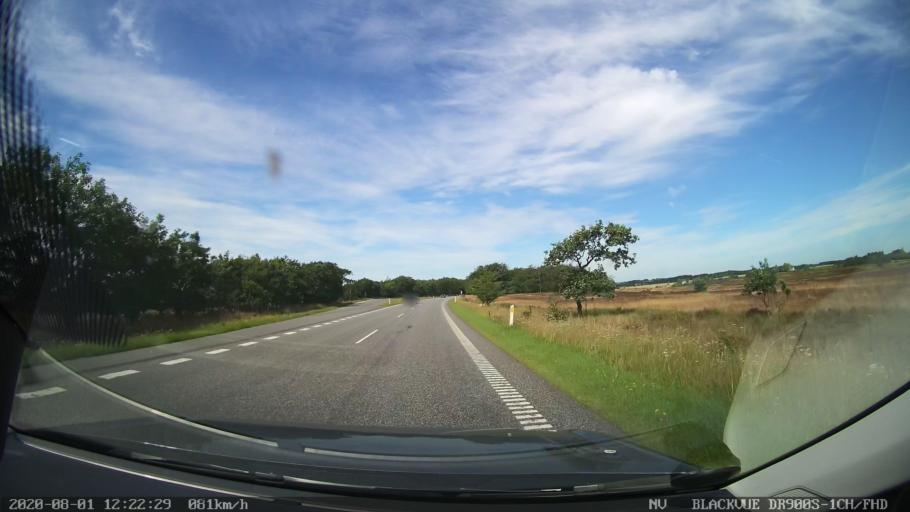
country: DK
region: Central Jutland
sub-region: Viborg Kommune
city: Karup
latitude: 56.3873
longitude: 9.1564
